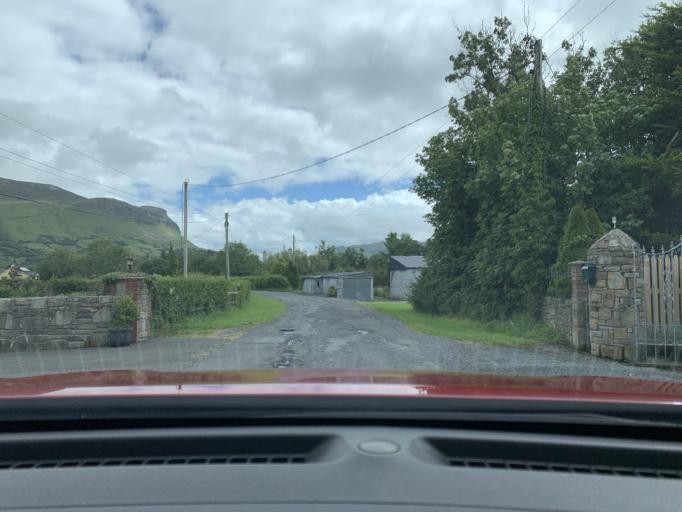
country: IE
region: Connaught
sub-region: Sligo
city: Sligo
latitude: 54.3353
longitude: -8.4956
